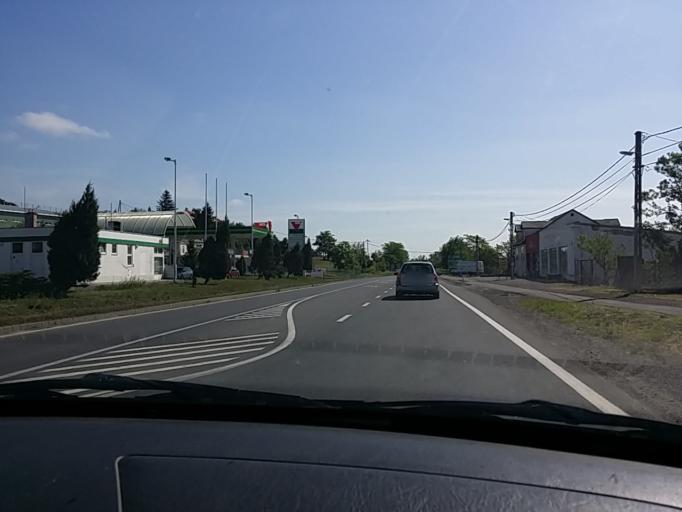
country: HU
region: Borsod-Abauj-Zemplen
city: Satoraljaujhely
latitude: 48.3776
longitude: 21.6383
